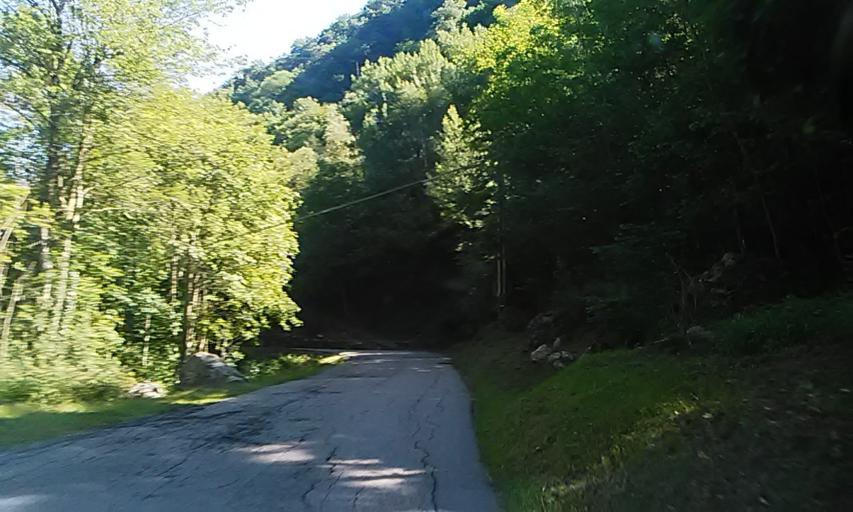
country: IT
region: Piedmont
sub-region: Provincia di Vercelli
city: Varallo
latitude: 45.8354
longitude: 8.2766
